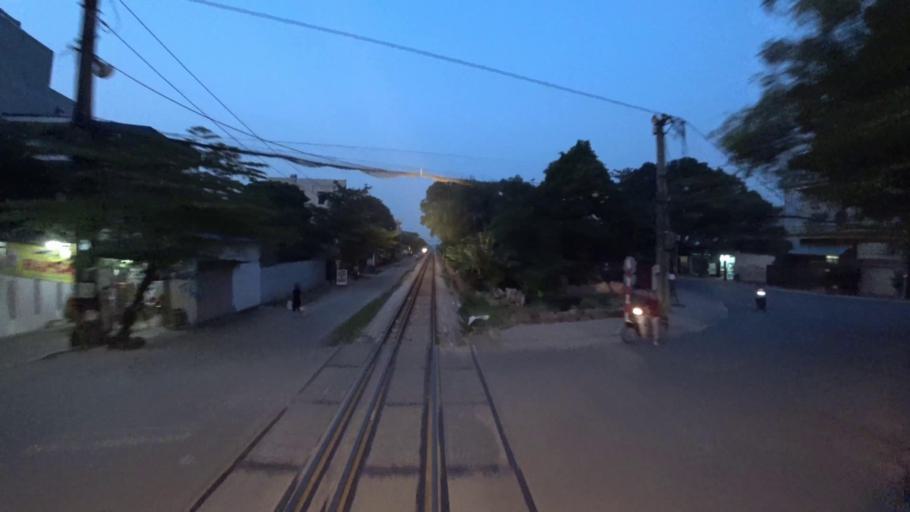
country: VN
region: Ha Noi
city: Soc Son
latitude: 21.2585
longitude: 105.8620
